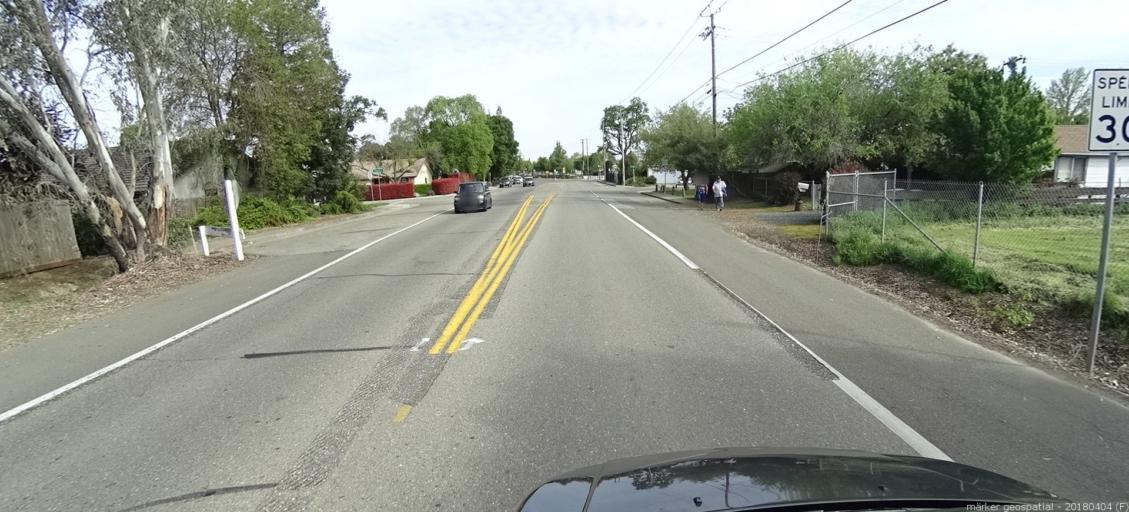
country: US
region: California
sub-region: Sacramento County
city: Galt
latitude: 38.2463
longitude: -121.2977
